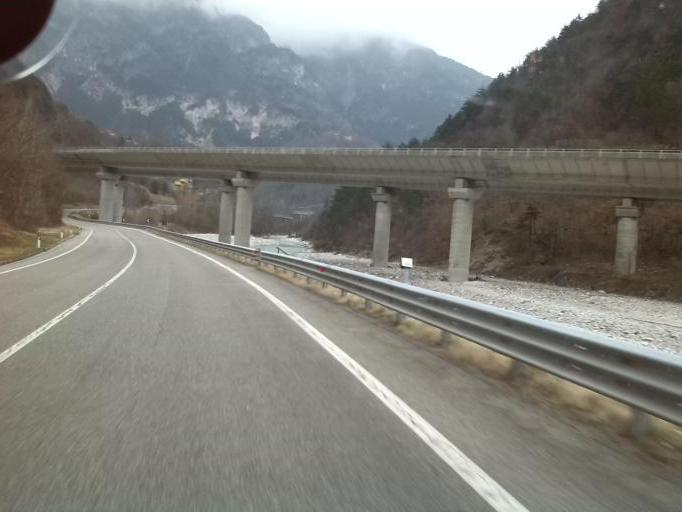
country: IT
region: Friuli Venezia Giulia
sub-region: Provincia di Udine
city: Dogna
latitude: 46.4385
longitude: 13.3092
